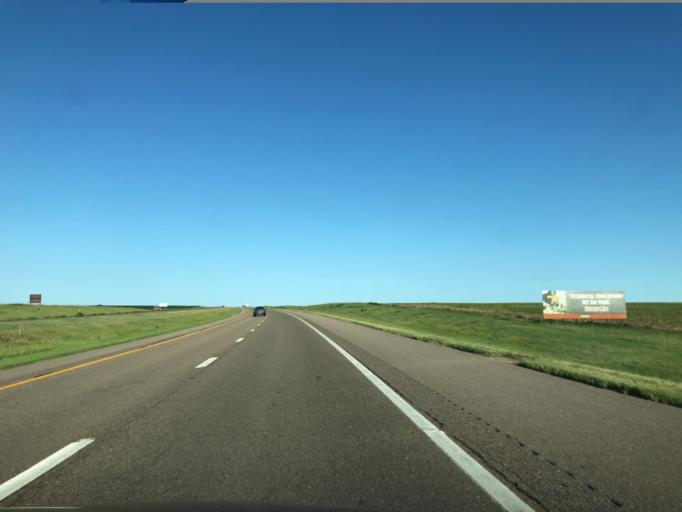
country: US
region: Kansas
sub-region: Trego County
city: WaKeeney
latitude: 39.0231
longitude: -99.9313
